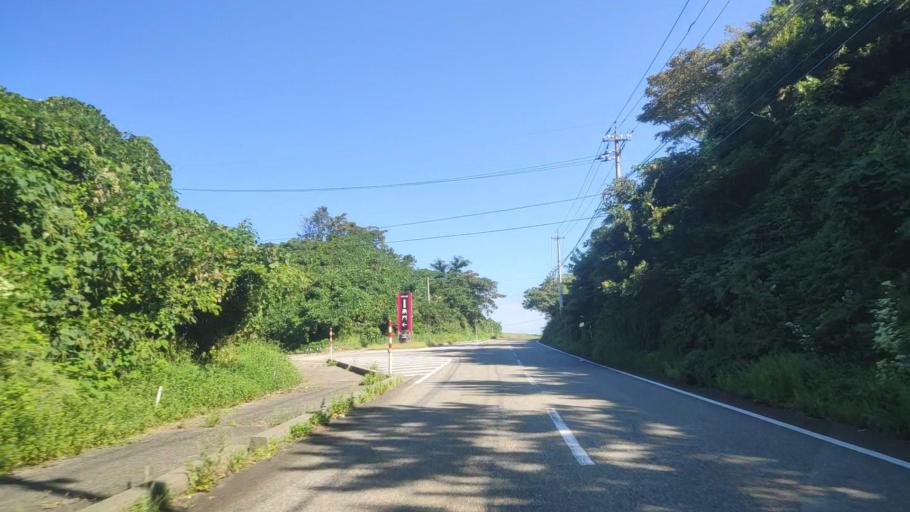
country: JP
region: Ishikawa
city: Hakui
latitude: 37.0944
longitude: 136.7294
